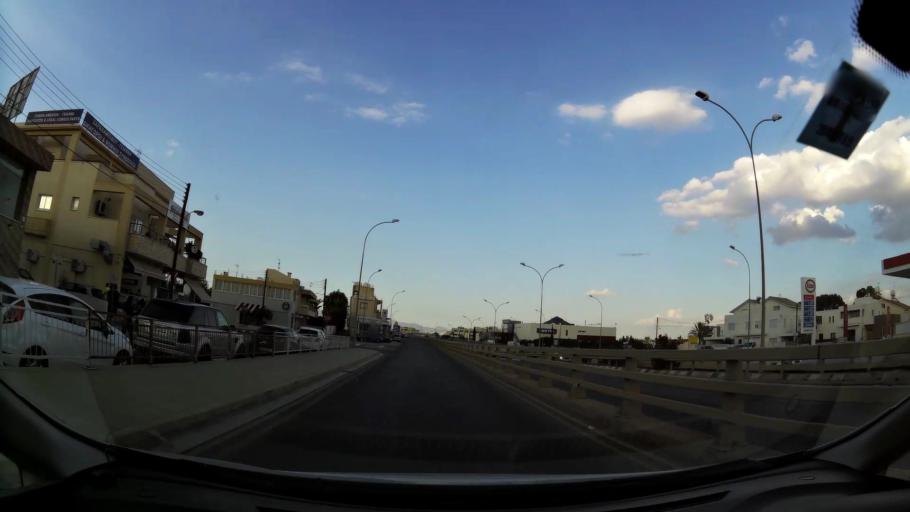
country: CY
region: Lefkosia
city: Tseri
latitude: 35.1240
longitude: 33.3217
